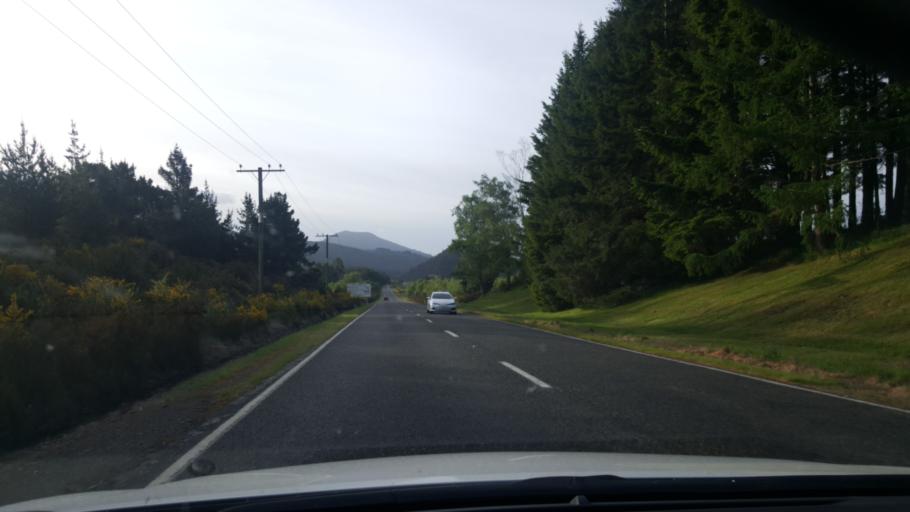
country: NZ
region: Waikato
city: Turangi
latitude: -38.9899
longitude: 175.7926
